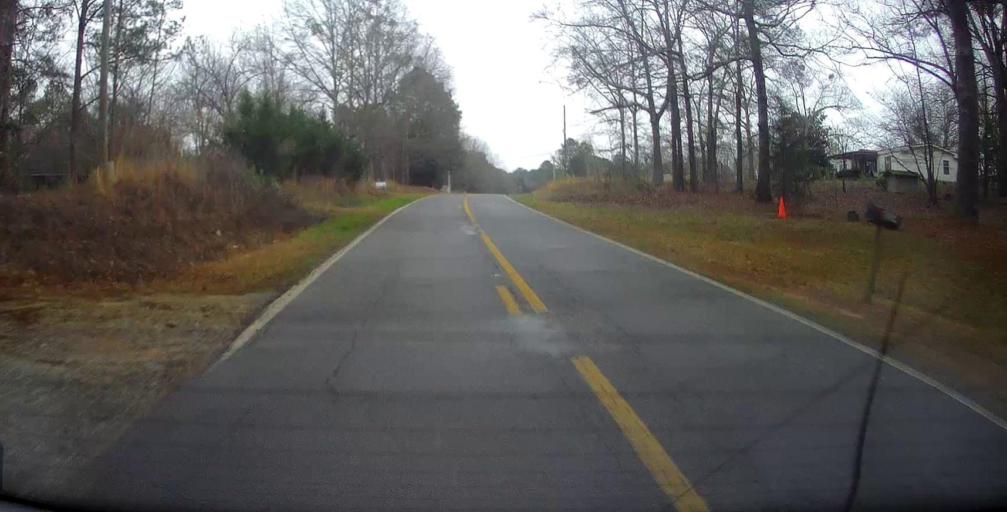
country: US
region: Georgia
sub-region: Monroe County
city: Forsyth
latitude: 33.1178
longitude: -83.9673
